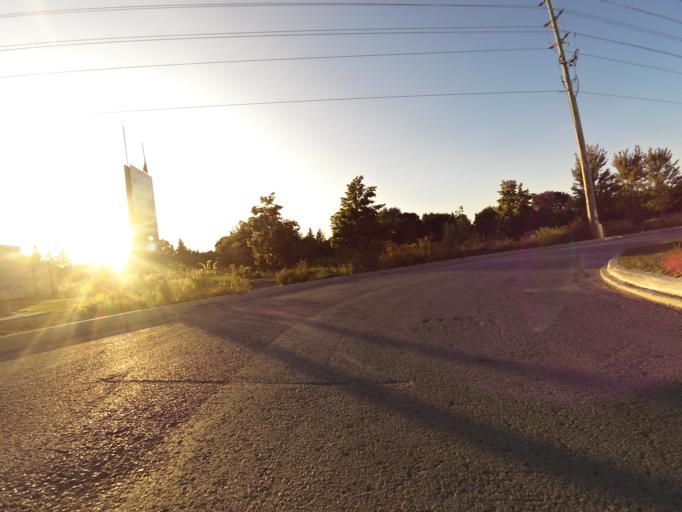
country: CA
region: Ontario
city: Bells Corners
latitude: 45.2872
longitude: -75.7449
